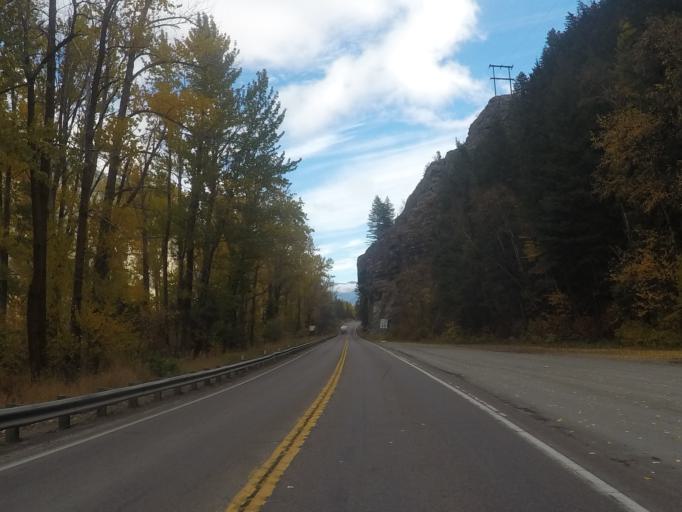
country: US
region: Montana
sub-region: Flathead County
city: Columbia Falls
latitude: 48.3858
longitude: -114.1023
